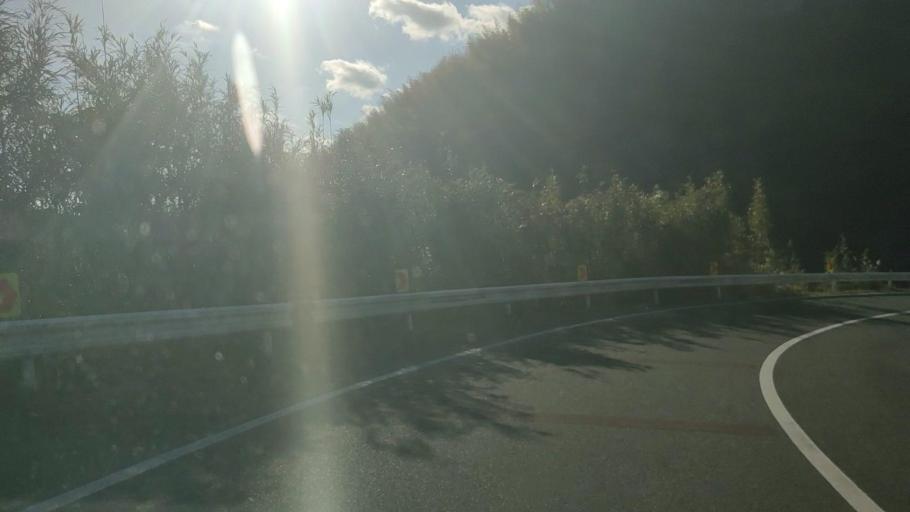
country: JP
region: Saga Prefecture
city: Kanzakimachi-kanzaki
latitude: 33.3914
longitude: 130.2673
